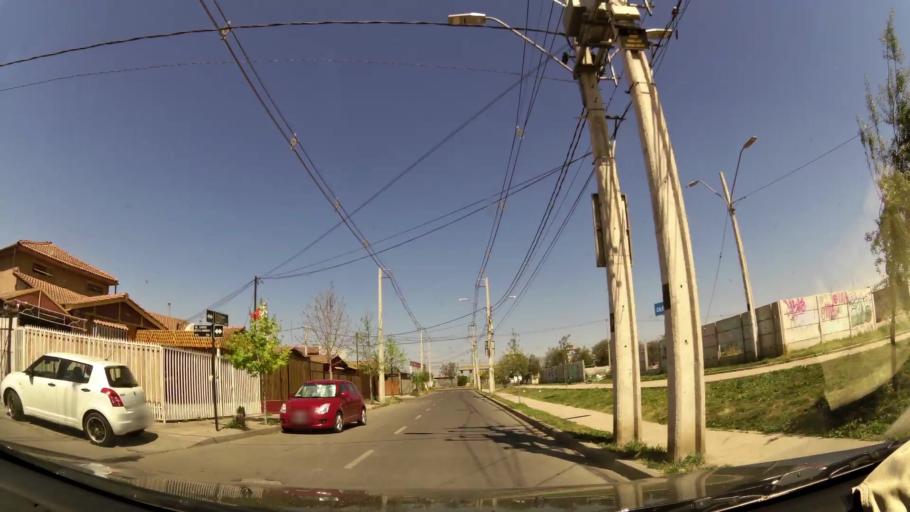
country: CL
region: Santiago Metropolitan
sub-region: Provincia de Santiago
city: Lo Prado
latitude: -33.3982
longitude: -70.7568
